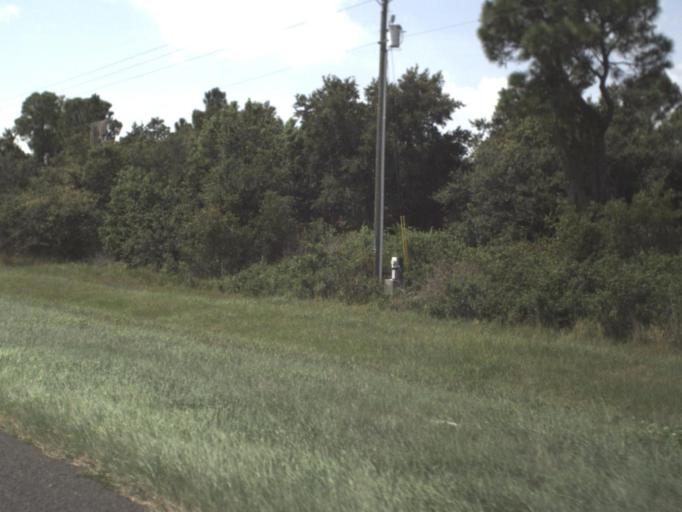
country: US
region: Florida
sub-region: Polk County
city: Crooked Lake Park
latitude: 27.8218
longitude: -81.5951
